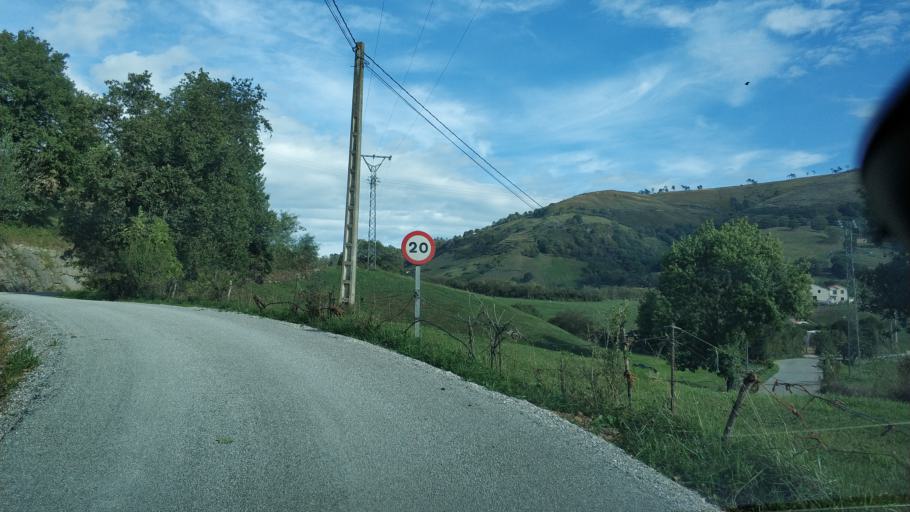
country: ES
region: Cantabria
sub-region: Provincia de Cantabria
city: Santa Maria de Cayon
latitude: 43.2837
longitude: -3.8022
